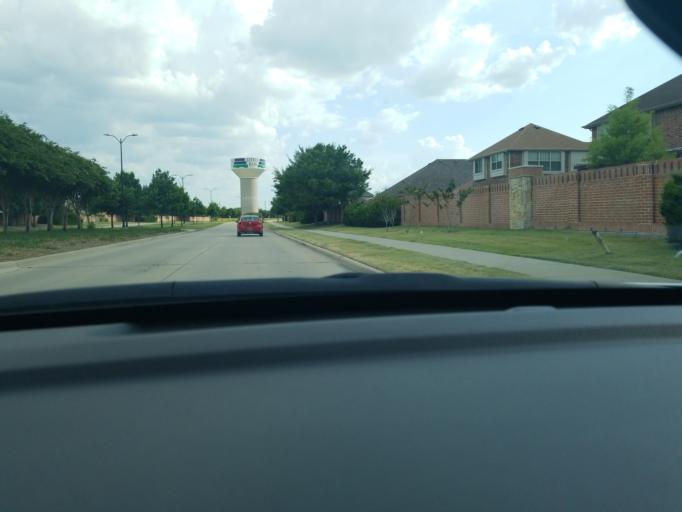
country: US
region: Texas
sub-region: Denton County
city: Little Elm
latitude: 33.1733
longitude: -96.8957
